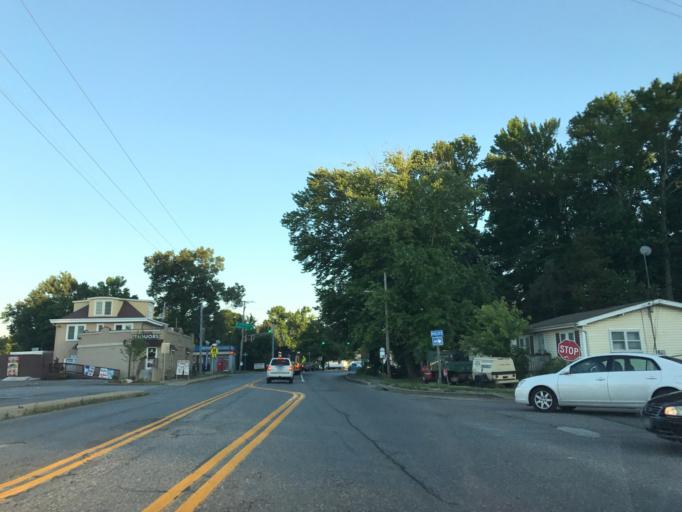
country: US
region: Maryland
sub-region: Anne Arundel County
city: Londontowne
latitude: 38.9313
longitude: -76.5567
